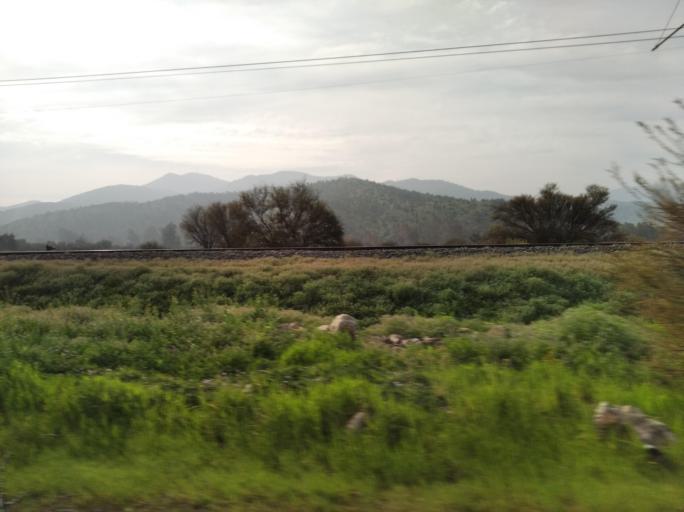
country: CL
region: Santiago Metropolitan
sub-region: Provincia de Chacabuco
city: Lampa
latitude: -33.1187
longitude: -70.9257
